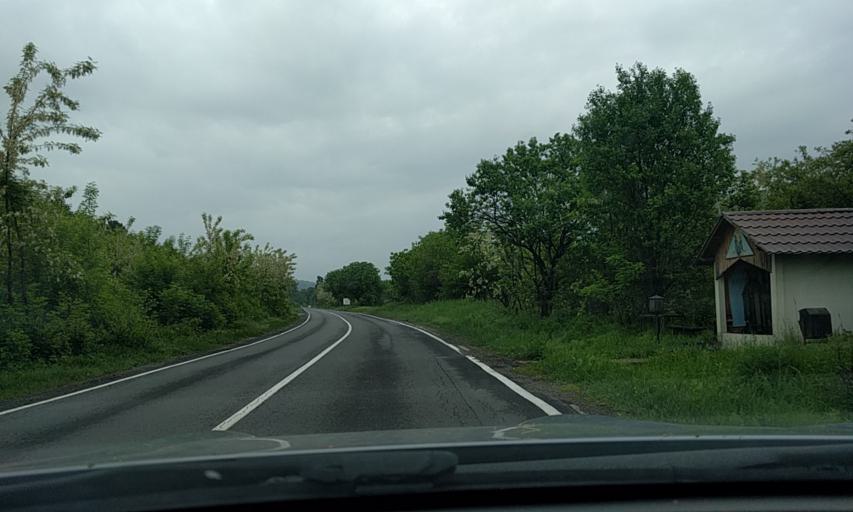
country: RO
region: Dambovita
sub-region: Comuna Branesti
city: Branesti
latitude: 45.0333
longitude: 25.4255
